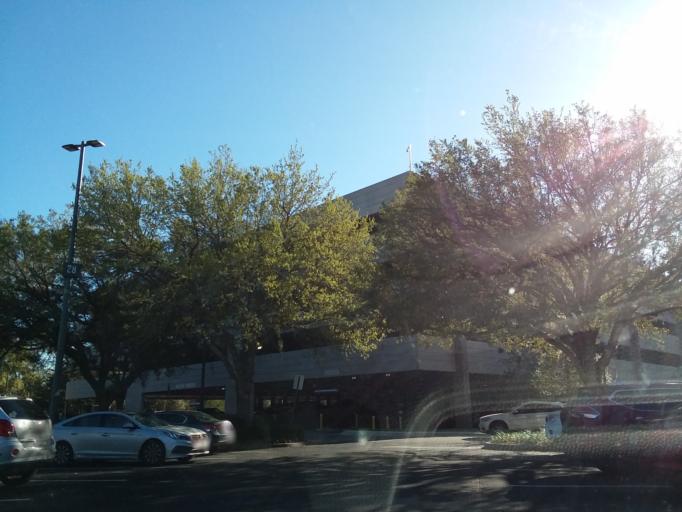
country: US
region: Florida
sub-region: Saint Johns County
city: Fruit Cove
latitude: 30.1924
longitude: -81.5535
